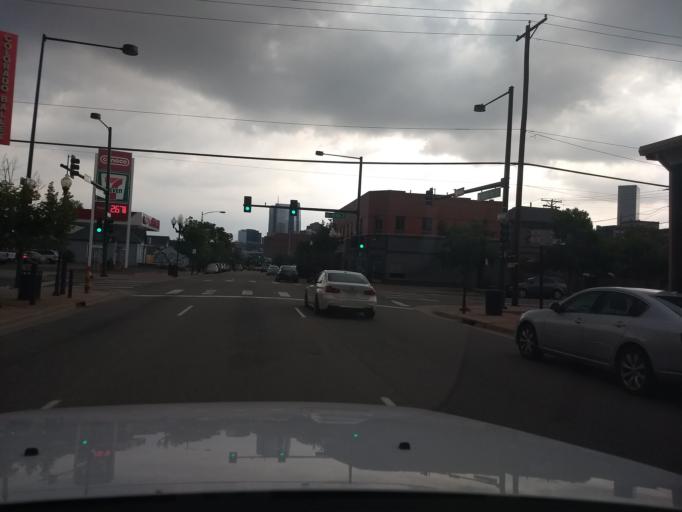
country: US
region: Colorado
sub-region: Denver County
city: Denver
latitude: 39.7334
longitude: -104.9987
